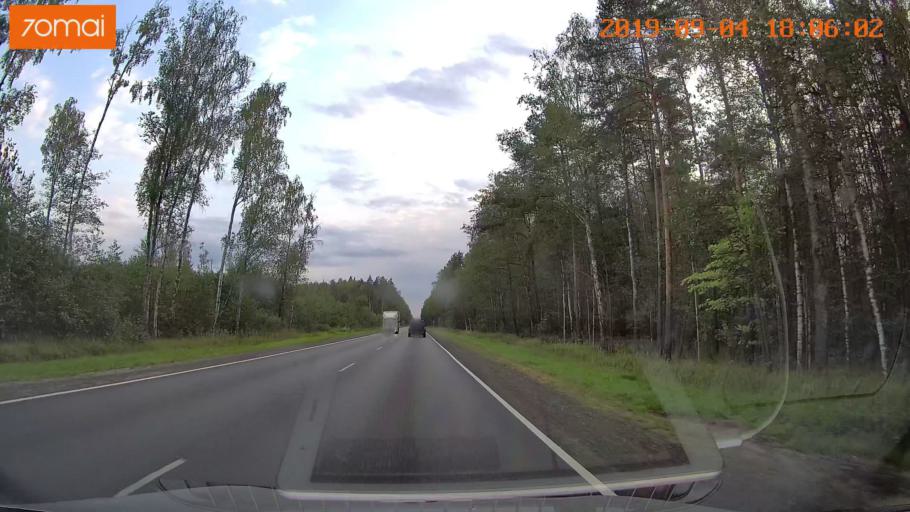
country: RU
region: Moskovskaya
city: Il'inskiy Pogost
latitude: 55.4351
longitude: 38.8194
